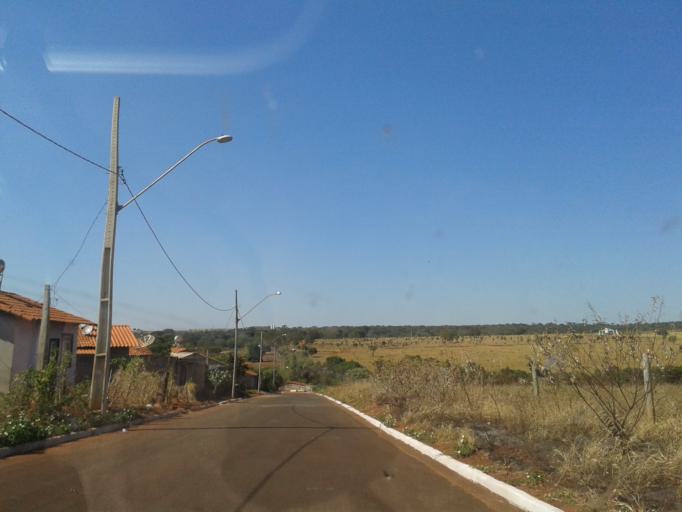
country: BR
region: Minas Gerais
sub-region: Ituiutaba
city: Ituiutaba
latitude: -19.0103
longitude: -49.4824
